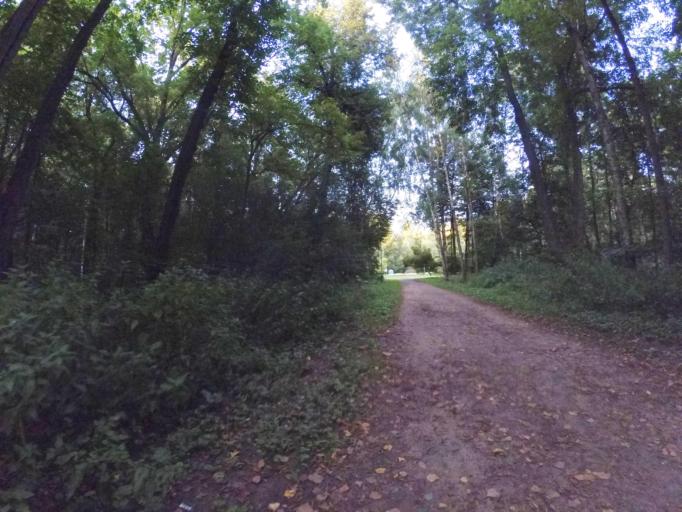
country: RU
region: Moscow
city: Kuz'minki
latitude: 55.6931
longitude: 37.7949
